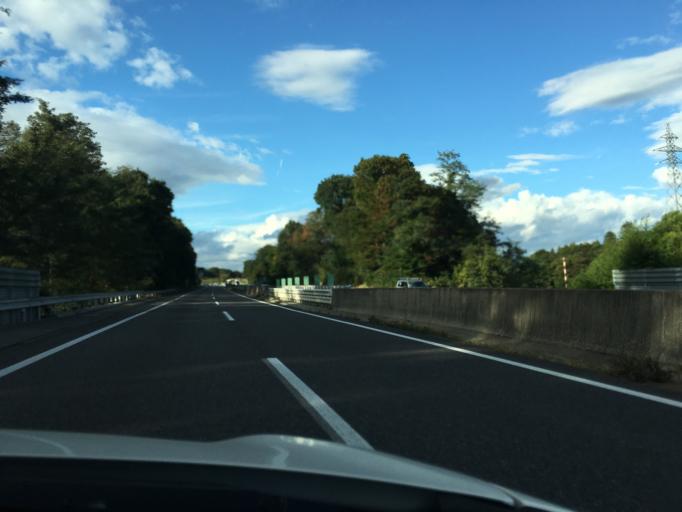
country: JP
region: Fukushima
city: Sukagawa
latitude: 37.3135
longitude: 140.3436
